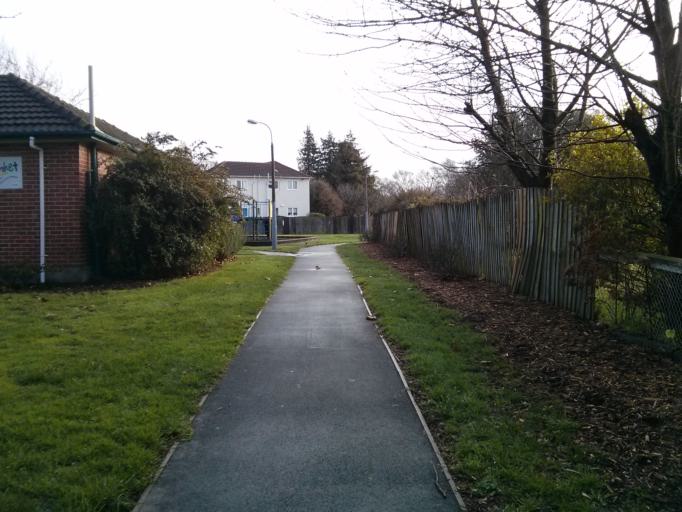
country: NZ
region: Canterbury
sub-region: Christchurch City
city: Christchurch
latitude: -43.5325
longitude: 172.5897
